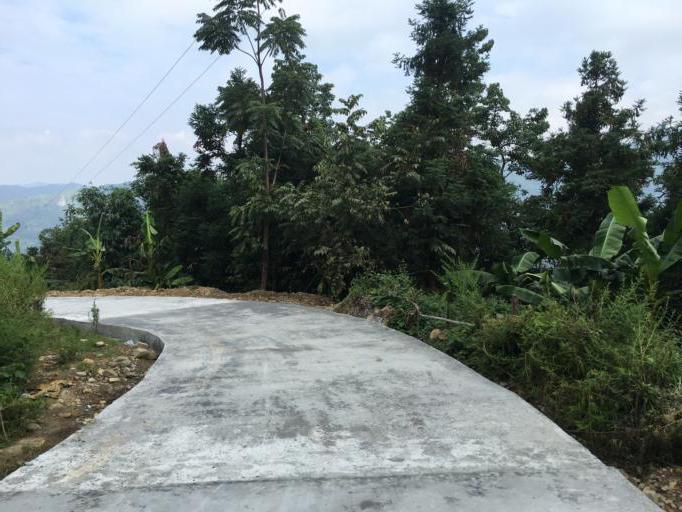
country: CN
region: Guangxi Zhuangzu Zizhiqu
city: Tongle
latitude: 25.2993
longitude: 106.1642
